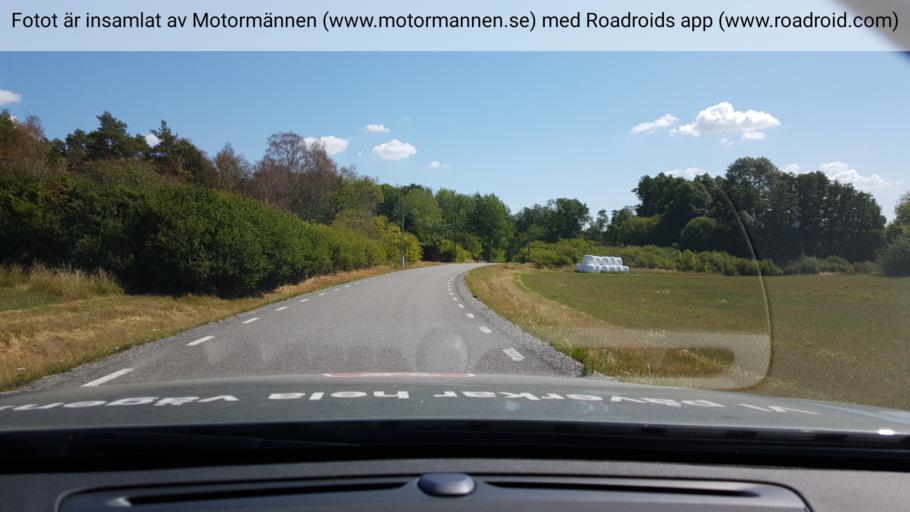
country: SE
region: Stockholm
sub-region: Upplands-Bro Kommun
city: Kungsaengen
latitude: 59.4072
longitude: 17.7167
